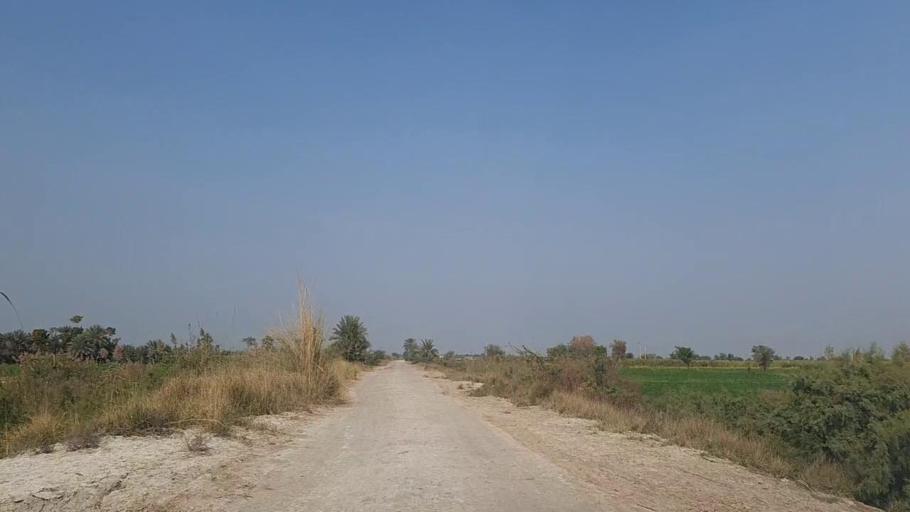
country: PK
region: Sindh
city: Daur
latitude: 26.4818
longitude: 68.4513
